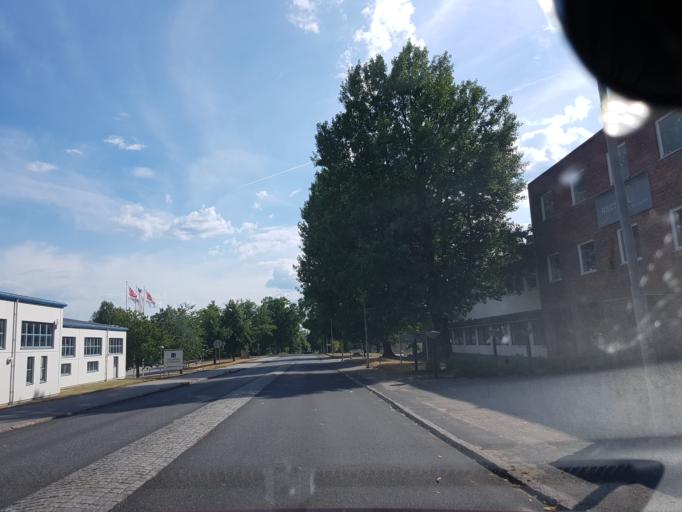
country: SE
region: Joenkoeping
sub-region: Gislaveds Kommun
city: Gislaved
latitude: 57.2969
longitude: 13.5288
